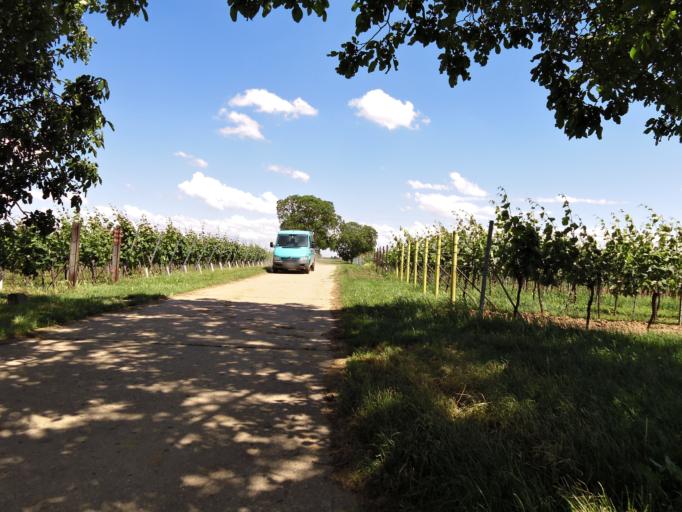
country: DE
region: Rheinland-Pfalz
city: Kleinfischlingen
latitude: 49.2675
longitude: 8.1889
